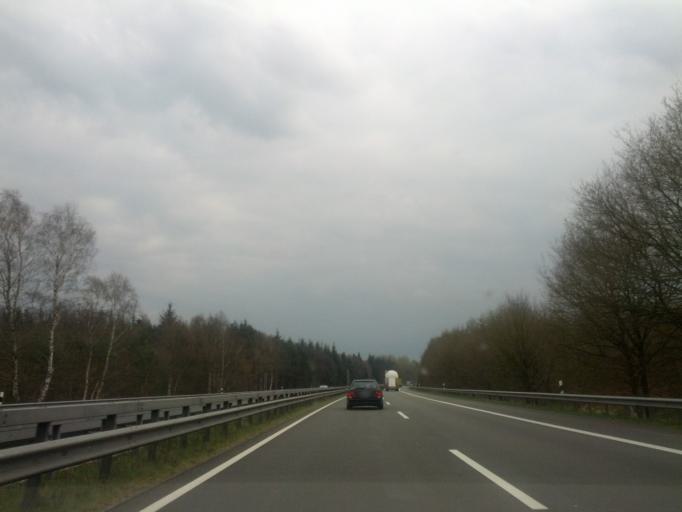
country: DE
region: Lower Saxony
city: Bad Zwischenahn
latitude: 53.2426
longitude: 8.0198
